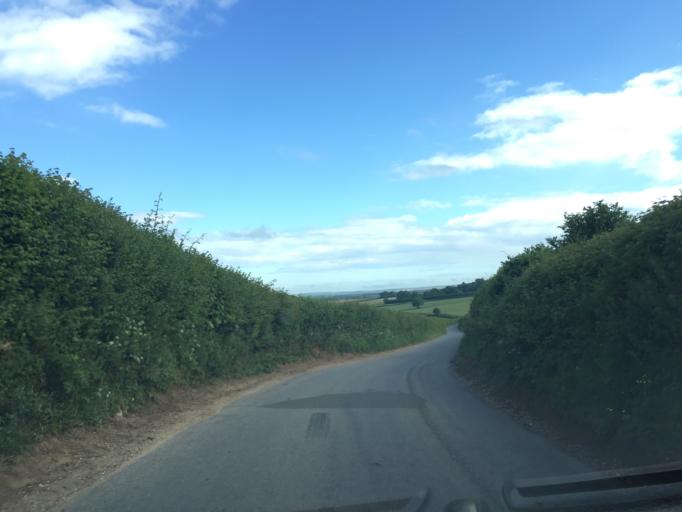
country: GB
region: England
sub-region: Dorset
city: Dorchester
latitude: 50.7444
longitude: -2.3377
